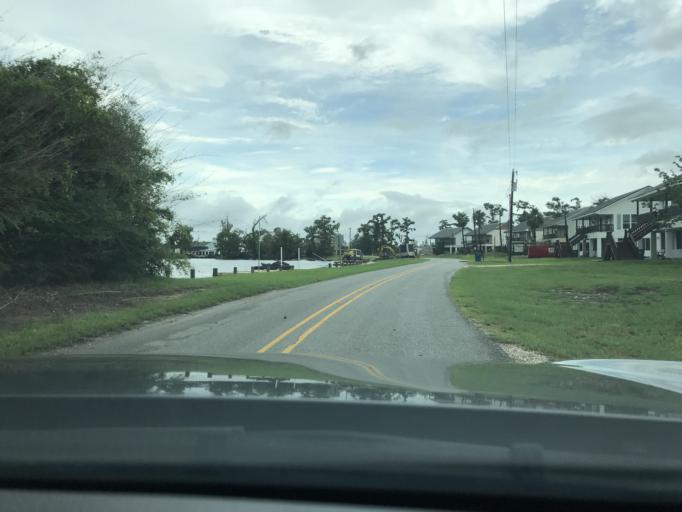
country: US
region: Louisiana
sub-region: Calcasieu Parish
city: Moss Bluff
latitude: 30.2739
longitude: -93.2208
